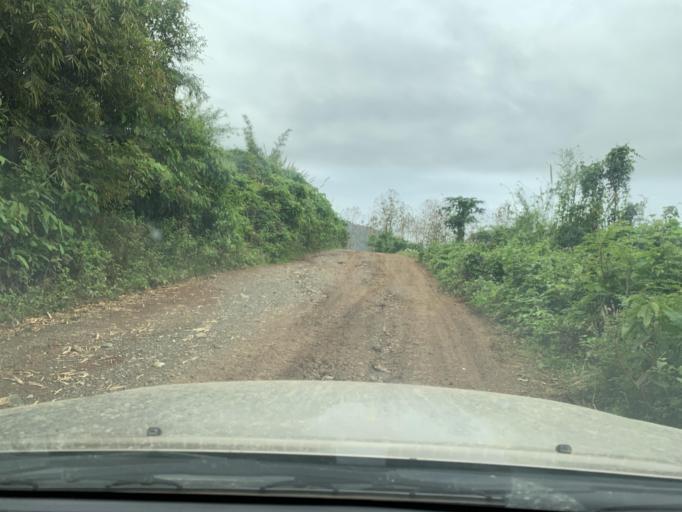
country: TH
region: Uttaradit
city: Ban Khok
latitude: 18.3993
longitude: 101.4306
